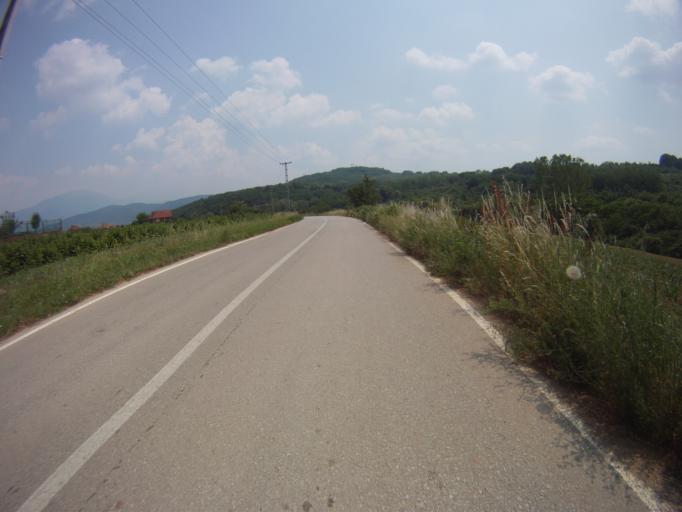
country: RS
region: Central Serbia
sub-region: Nisavski Okrug
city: Gadzin Han
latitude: 43.2056
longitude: 21.9904
